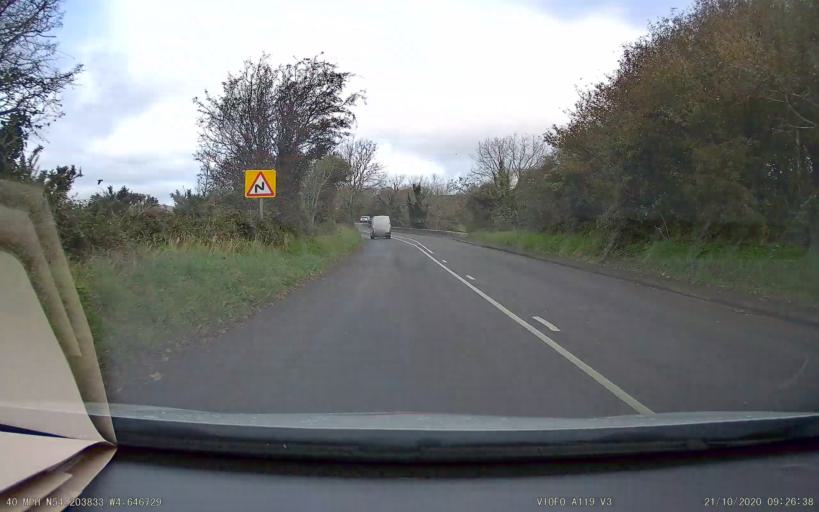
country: IM
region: Castletown
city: Castletown
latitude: 54.2038
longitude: -4.6467
